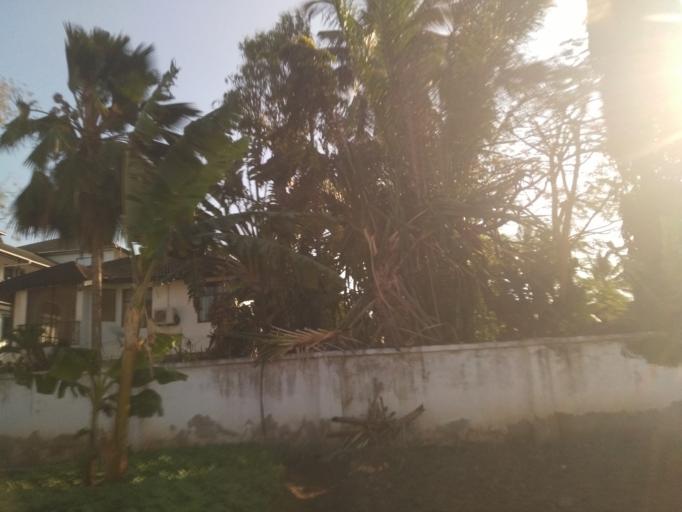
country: TZ
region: Dar es Salaam
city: Magomeni
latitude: -6.7645
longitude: 39.2559
